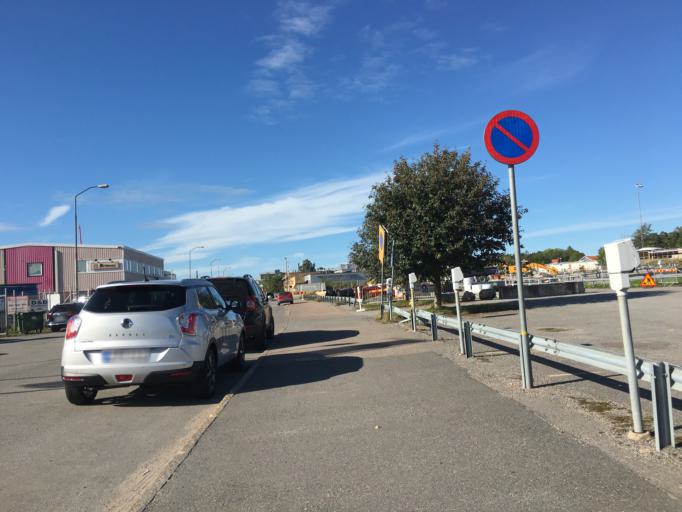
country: SE
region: Uppsala
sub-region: Uppsala Kommun
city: Uppsala
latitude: 59.8508
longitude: 17.6724
